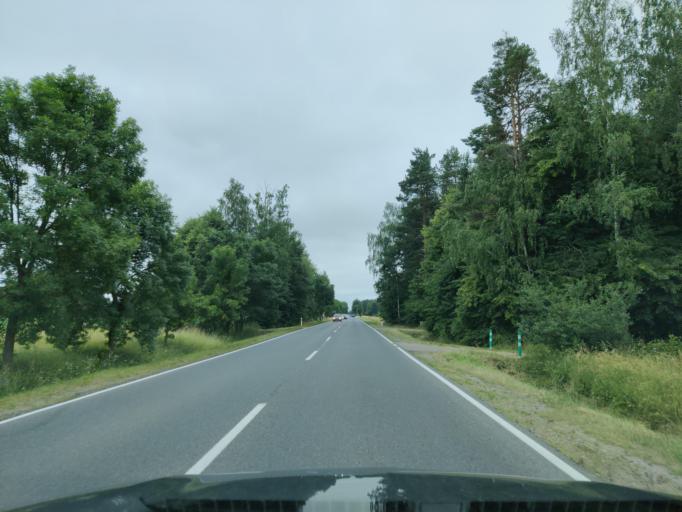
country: PL
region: Masovian Voivodeship
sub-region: Powiat ostrolecki
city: Myszyniec
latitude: 53.4209
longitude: 21.3553
